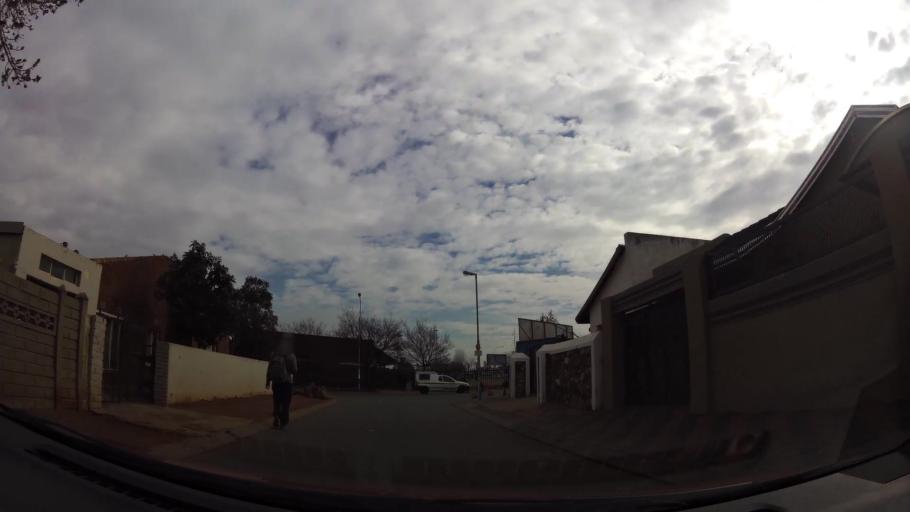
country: ZA
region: Gauteng
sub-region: City of Johannesburg Metropolitan Municipality
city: Soweto
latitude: -26.2731
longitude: 27.8324
